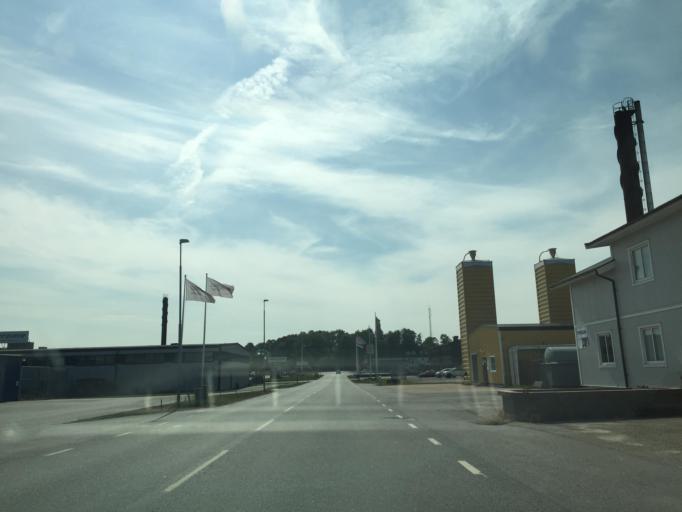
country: SE
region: Vaestra Goetaland
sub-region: Tanums Kommun
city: Tanumshede
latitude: 58.7280
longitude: 11.3338
